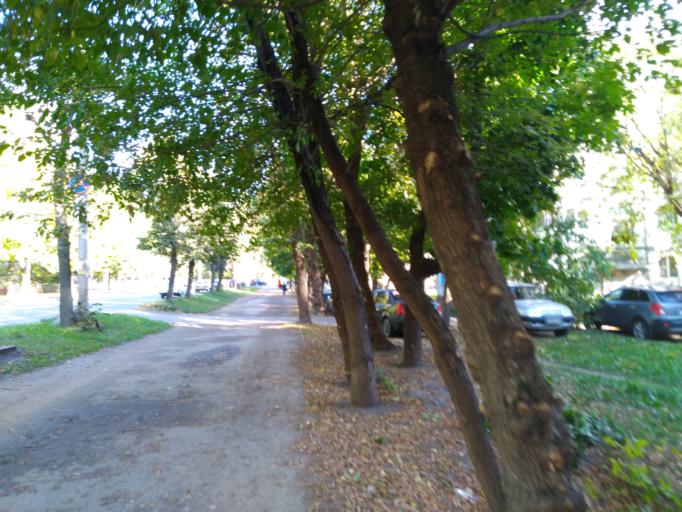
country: RU
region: Kaluga
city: Kaluga
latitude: 54.5295
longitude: 36.2726
